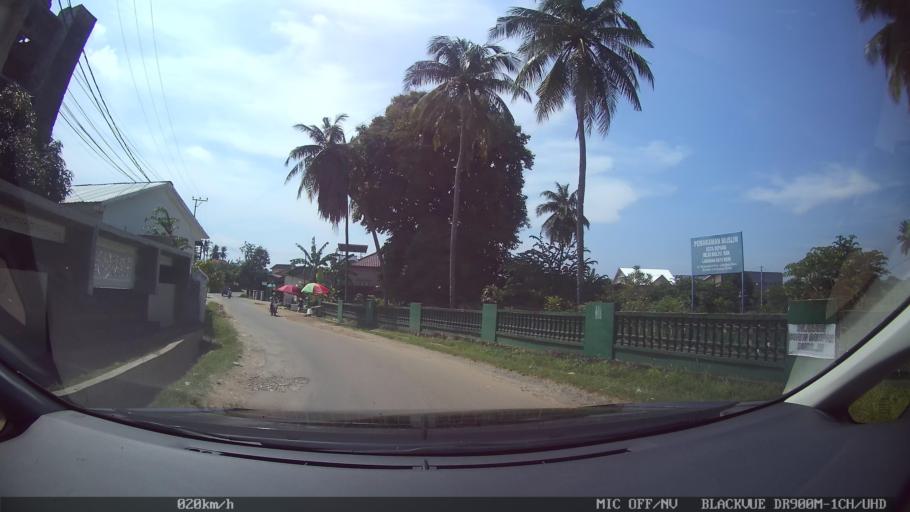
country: ID
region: Lampung
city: Kedaton
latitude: -5.3776
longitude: 105.2604
